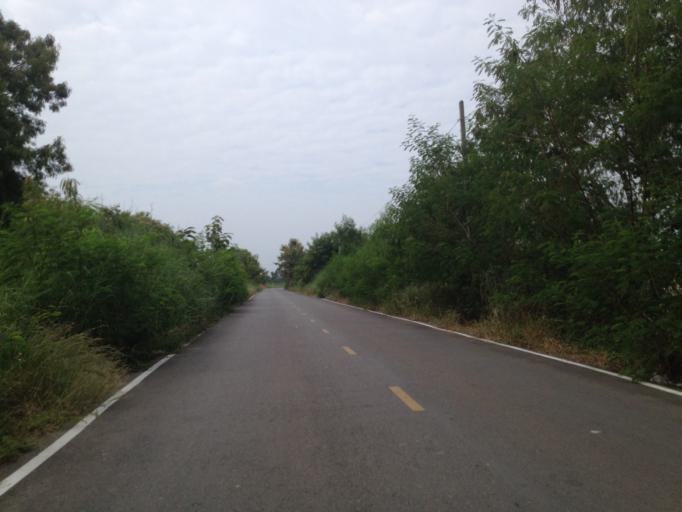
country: TH
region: Chiang Mai
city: San Pa Tong
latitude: 18.6560
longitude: 98.8986
